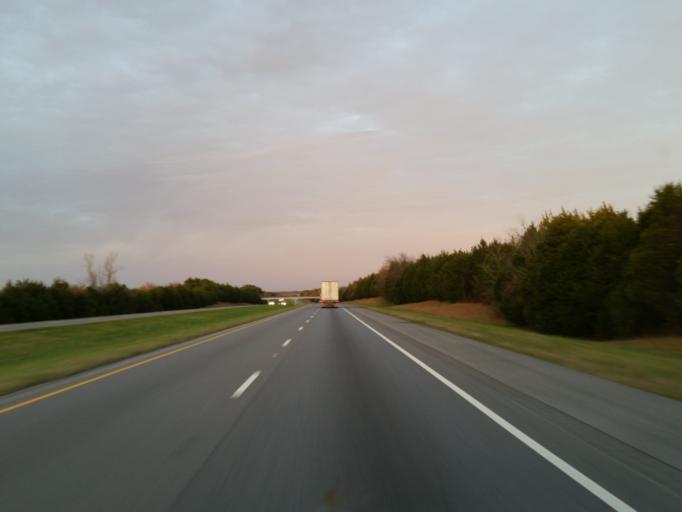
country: US
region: Alabama
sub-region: Sumter County
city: Livingston
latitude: 32.6661
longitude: -88.1767
